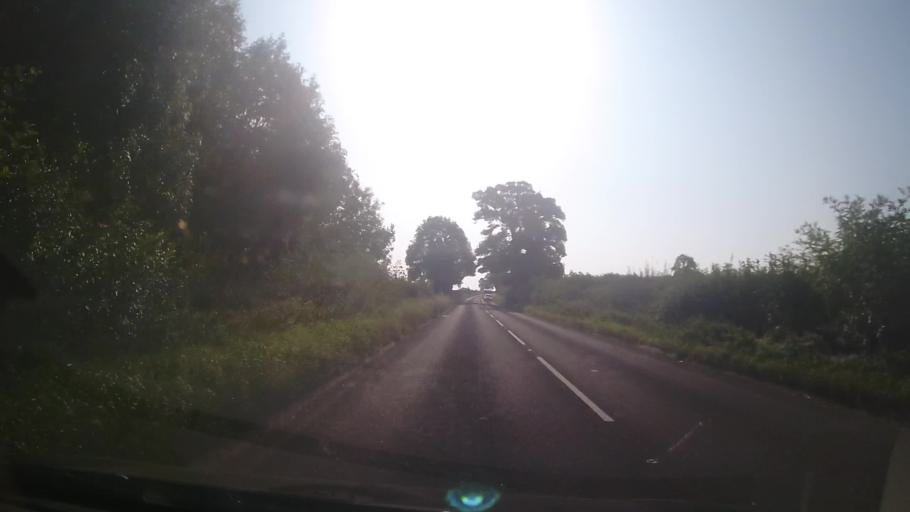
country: GB
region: England
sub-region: Shropshire
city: Much Wenlock
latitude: 52.5902
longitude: -2.5548
